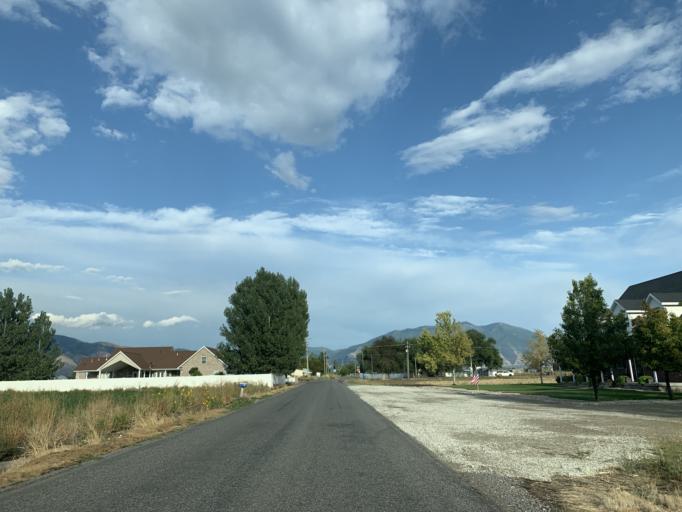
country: US
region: Utah
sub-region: Utah County
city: Benjamin
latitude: 40.1292
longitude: -111.7322
